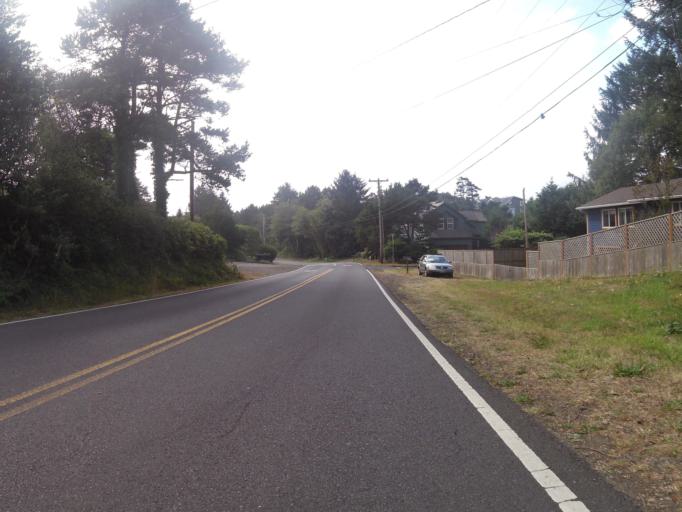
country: US
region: Oregon
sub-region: Lincoln County
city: Newport
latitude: 44.6527
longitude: -124.0567
